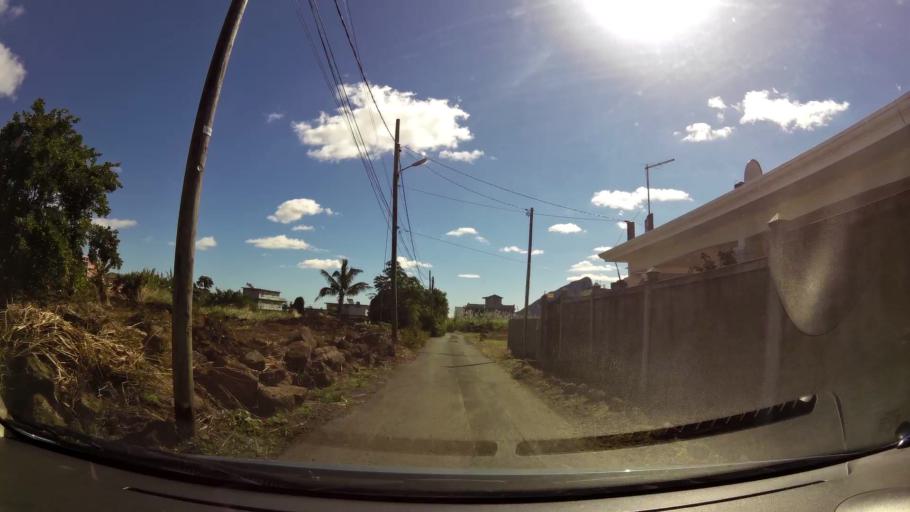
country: MU
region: Plaines Wilhems
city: Vacoas
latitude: -20.2913
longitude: 57.4745
